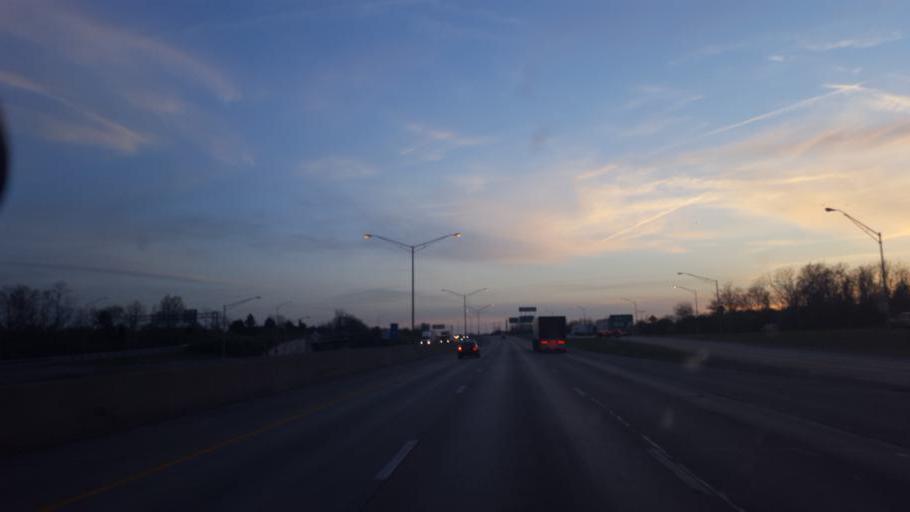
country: US
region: Kentucky
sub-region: Kenton County
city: Erlanger
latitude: 39.0334
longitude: -84.6032
